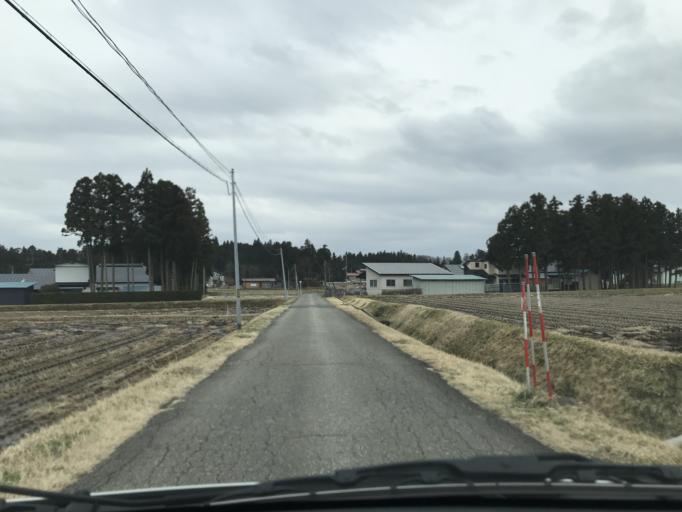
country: JP
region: Iwate
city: Kitakami
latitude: 39.2211
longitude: 141.0765
